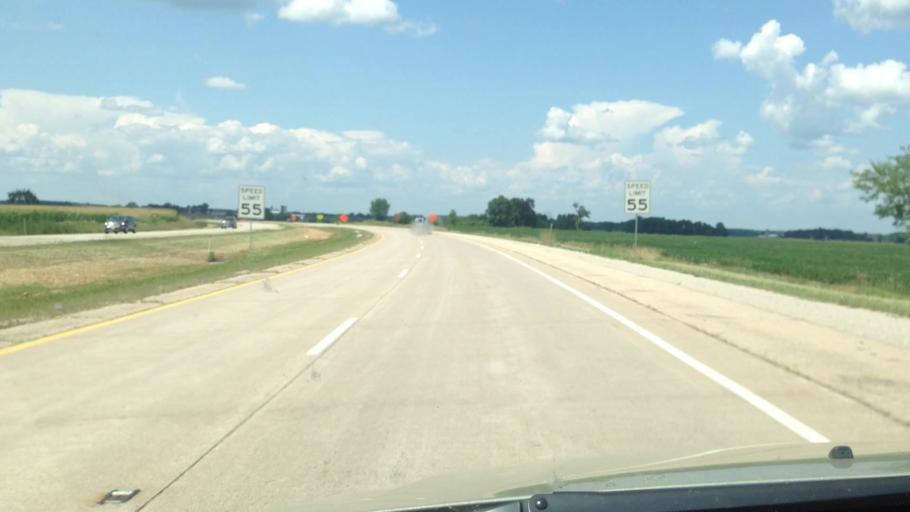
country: US
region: Wisconsin
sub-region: Brown County
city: Pulaski
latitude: 44.6816
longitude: -88.3119
